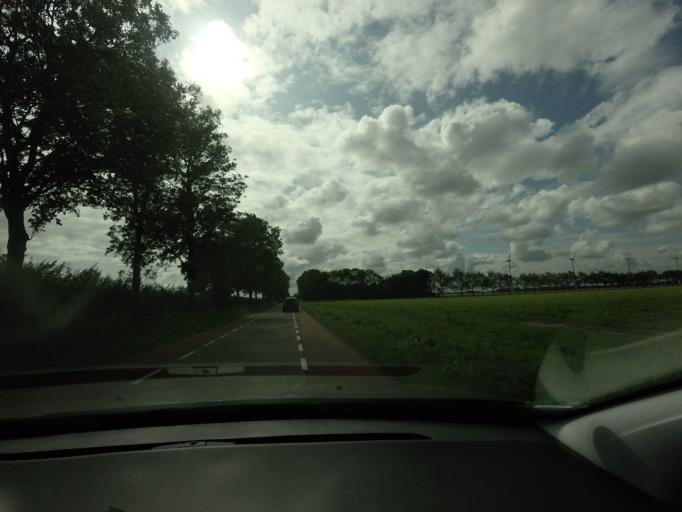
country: NL
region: North Holland
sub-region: Gemeente Medemblik
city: Medemblik
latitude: 52.8094
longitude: 5.1071
